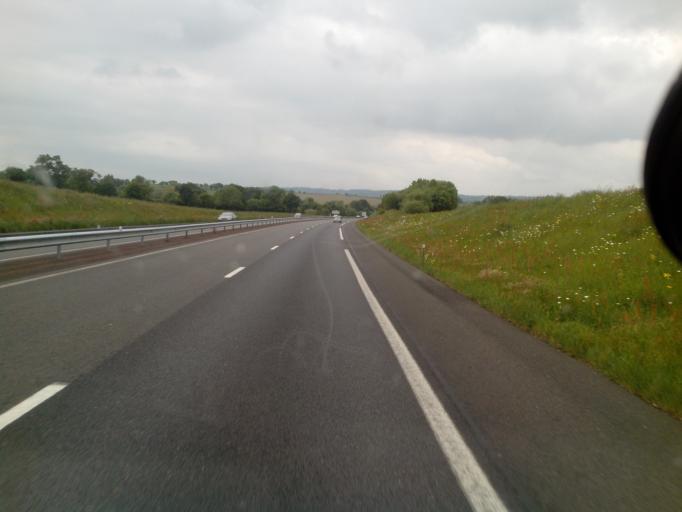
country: FR
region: Lower Normandy
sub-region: Departement de la Manche
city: Saint-Quentin-sur-le-Homme
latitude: 48.6071
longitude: -1.3337
